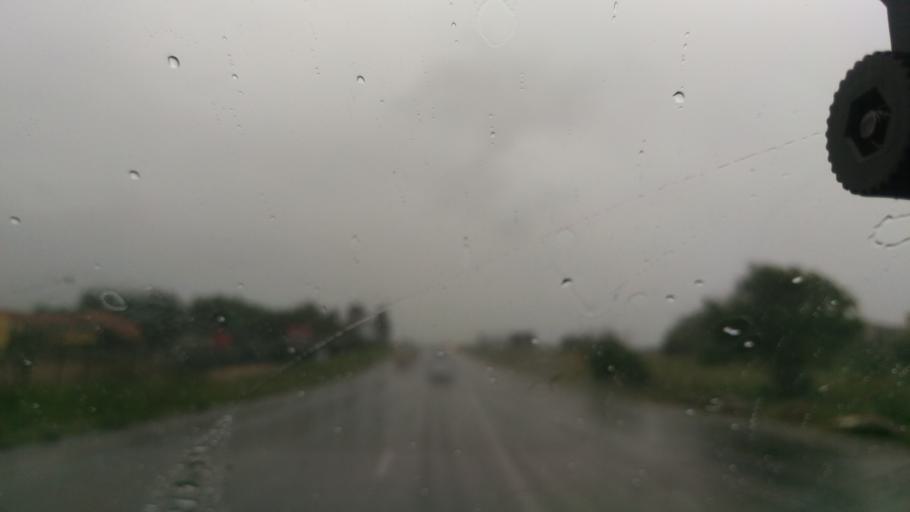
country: ZA
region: Gauteng
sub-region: City of Johannesburg Metropolitan Municipality
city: Diepsloot
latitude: -26.0302
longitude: 27.9725
